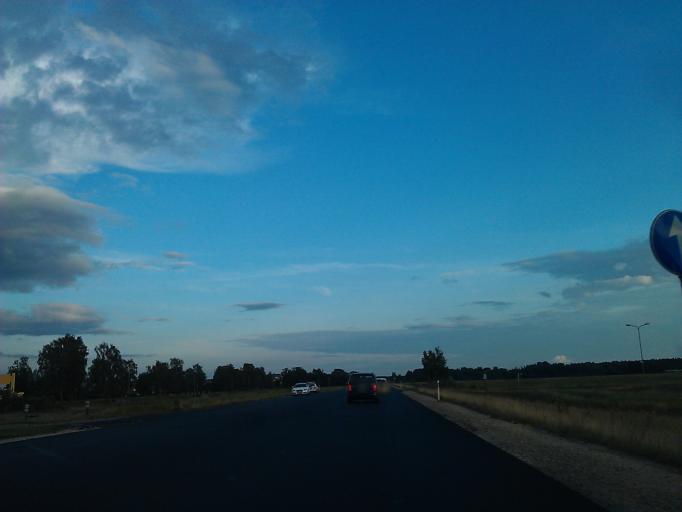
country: LV
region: Adazi
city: Adazi
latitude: 57.0893
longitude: 24.3134
